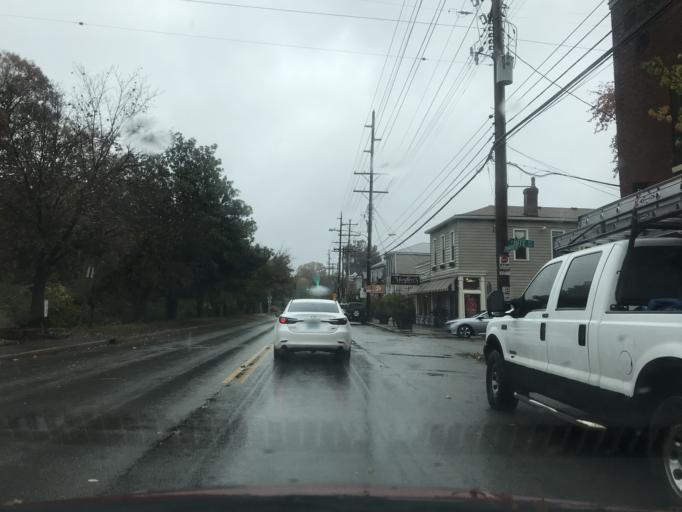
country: US
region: Kentucky
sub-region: Jefferson County
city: Indian Hills
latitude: 38.2545
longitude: -85.6943
